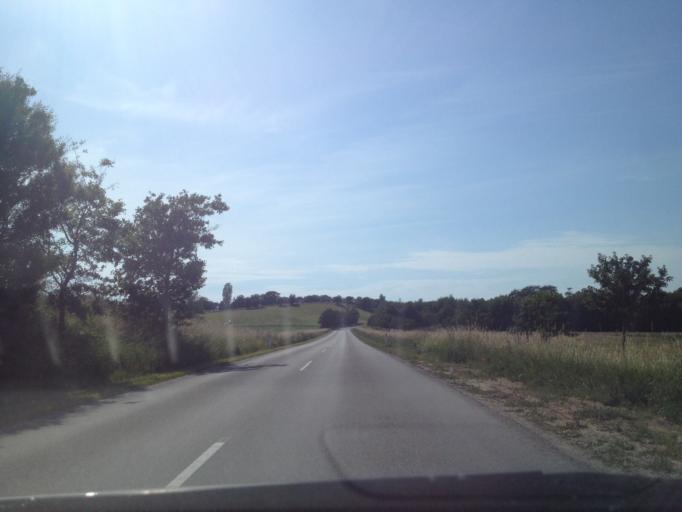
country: DK
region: Central Jutland
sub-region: Samso Kommune
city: Tranebjerg
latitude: 55.8594
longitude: 10.5705
